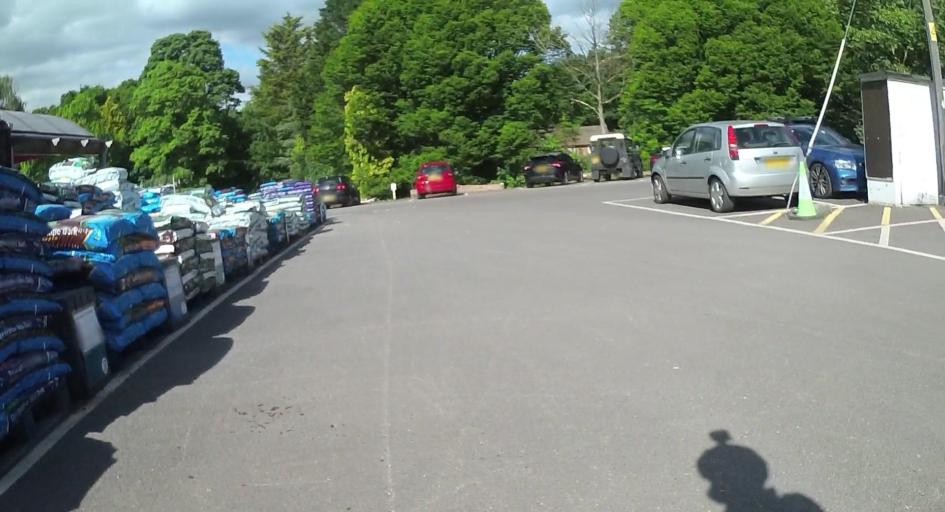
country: GB
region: England
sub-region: Surrey
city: Farnham
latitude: 51.1786
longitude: -0.7776
